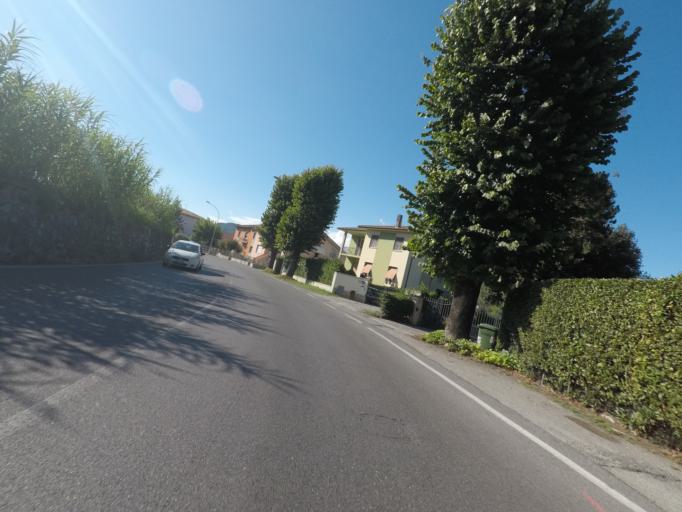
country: IT
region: Tuscany
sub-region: Provincia di Lucca
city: Lucca
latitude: 43.8703
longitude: 10.5067
